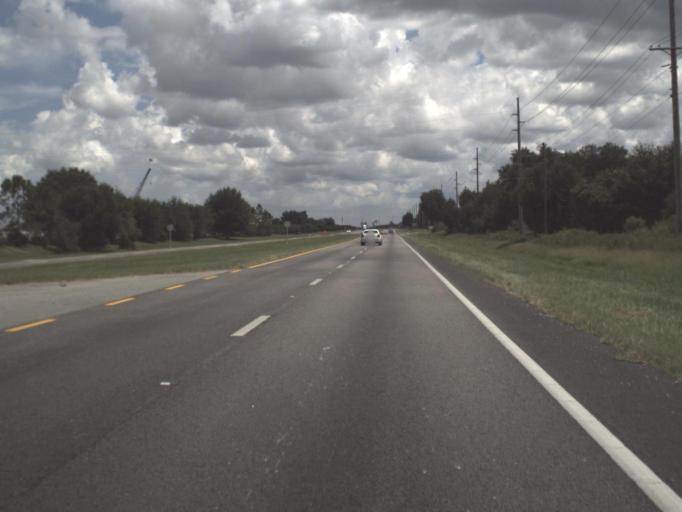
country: US
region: Florida
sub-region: Polk County
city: Alturas
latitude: 27.9028
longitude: -81.6583
